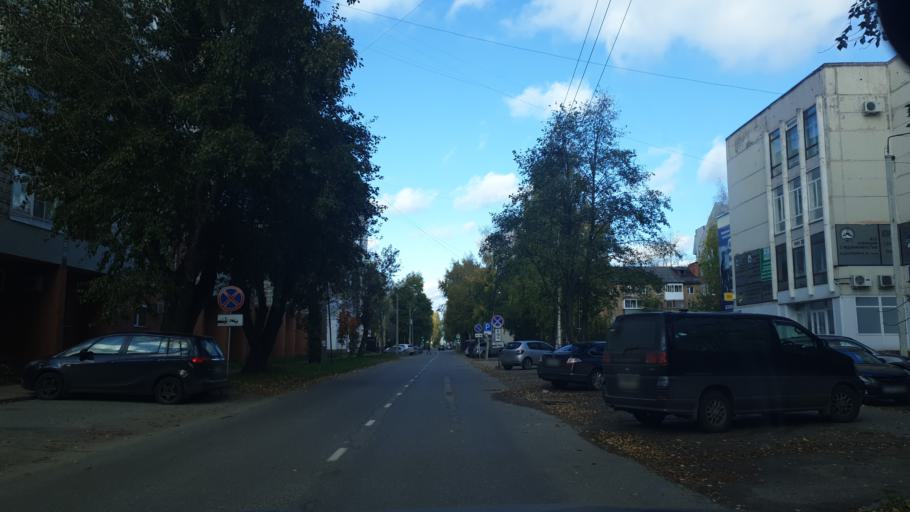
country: RU
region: Komi Republic
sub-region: Syktyvdinskiy Rayon
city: Syktyvkar
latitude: 61.6641
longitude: 50.8449
